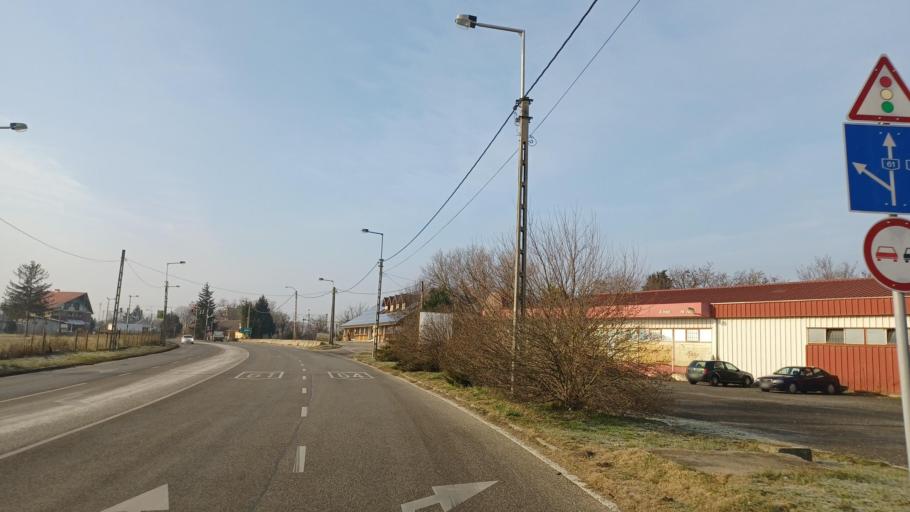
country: HU
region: Tolna
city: Simontornya
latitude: 46.7578
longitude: 18.5447
